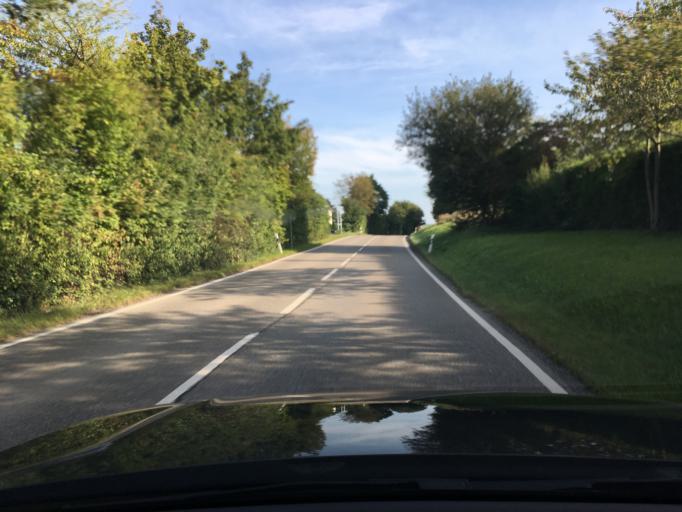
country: DE
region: Baden-Wuerttemberg
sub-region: Regierungsbezirk Stuttgart
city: Affalterbach
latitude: 48.9196
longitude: 9.3309
